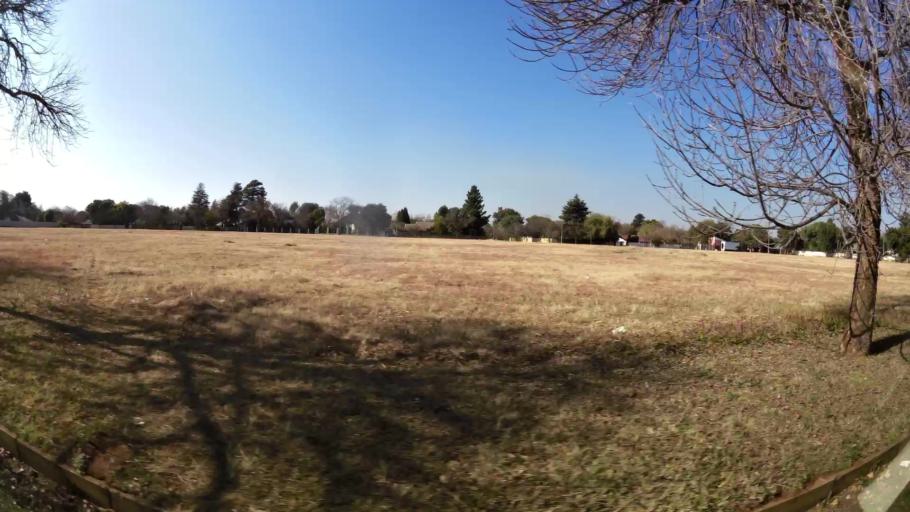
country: ZA
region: Gauteng
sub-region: Ekurhuleni Metropolitan Municipality
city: Benoni
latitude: -26.1423
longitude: 28.3385
